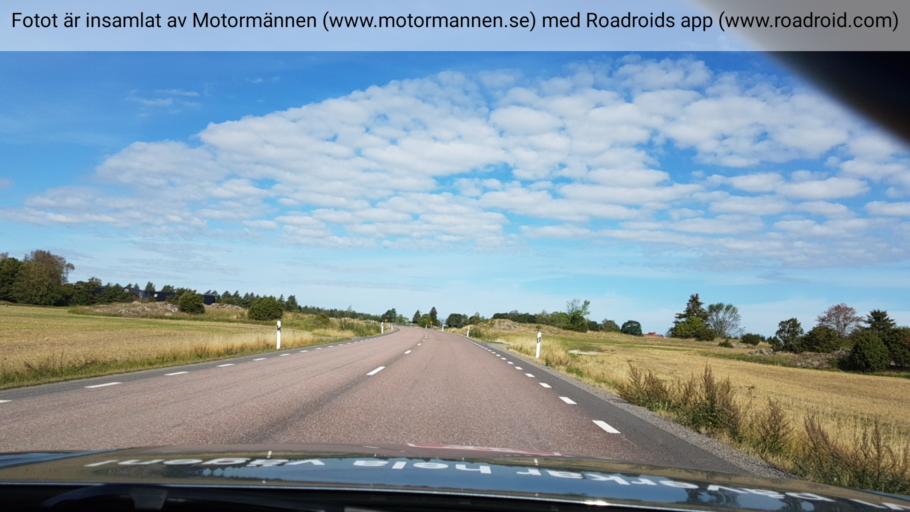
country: SE
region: Uppsala
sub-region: Osthammars Kommun
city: Bjorklinge
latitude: 59.9275
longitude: 17.4947
